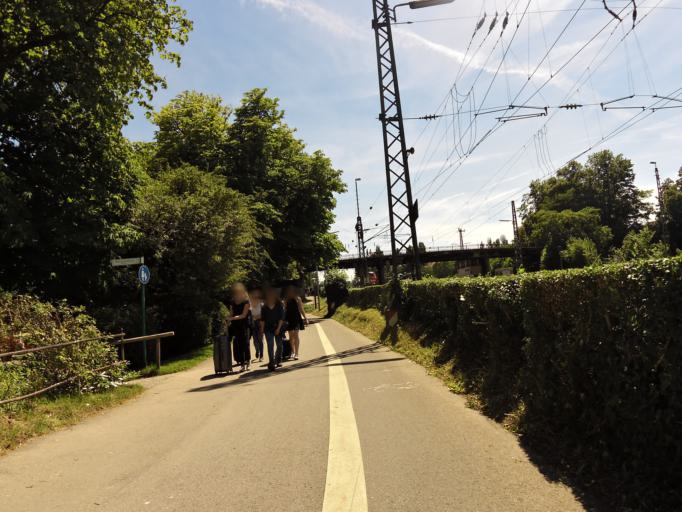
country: DE
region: Bavaria
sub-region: Swabia
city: Lindau
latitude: 47.5487
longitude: 9.6812
